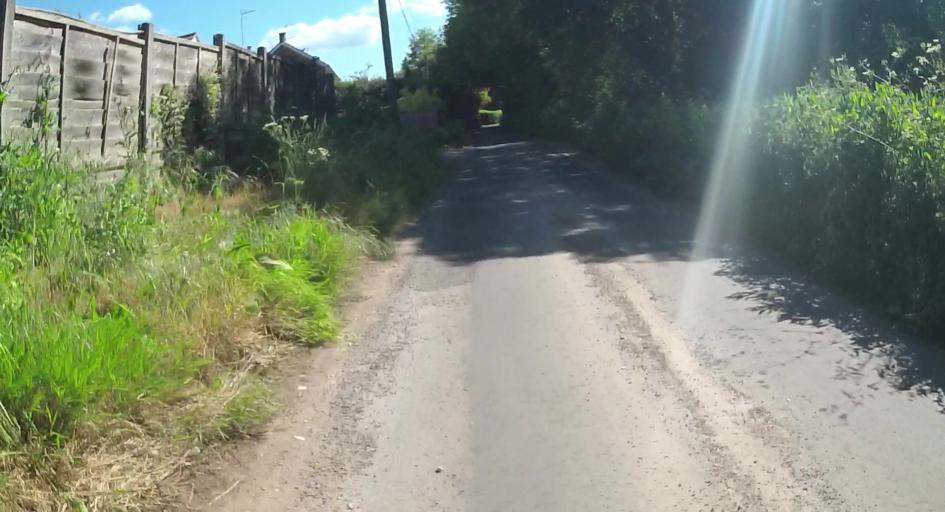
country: GB
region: England
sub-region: Hampshire
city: Old Basing
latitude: 51.2575
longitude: -1.0153
